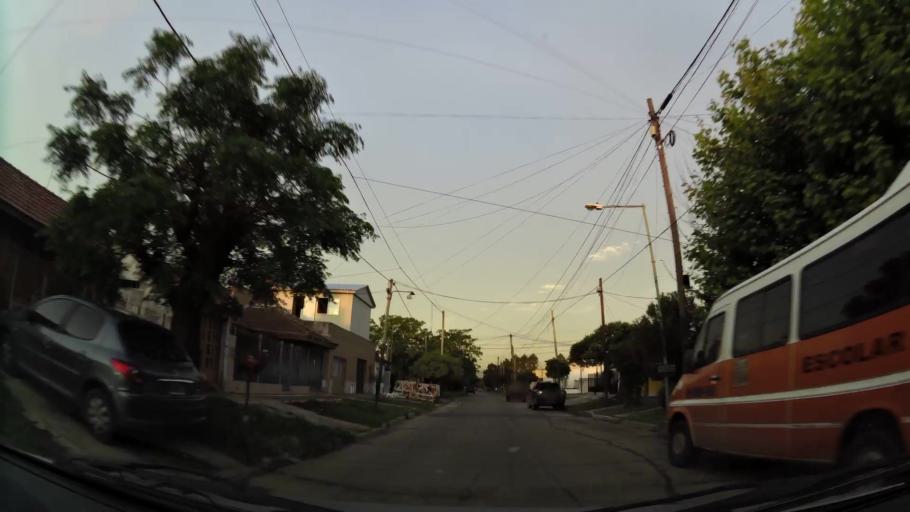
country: AR
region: Buenos Aires
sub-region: Partido de Lomas de Zamora
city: Lomas de Zamora
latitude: -34.7694
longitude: -58.3811
